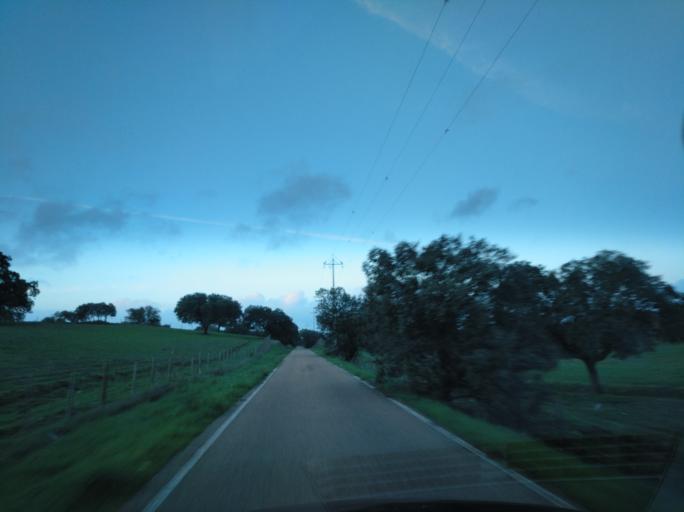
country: PT
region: Portalegre
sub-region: Campo Maior
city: Campo Maior
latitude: 39.0792
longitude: -7.1166
